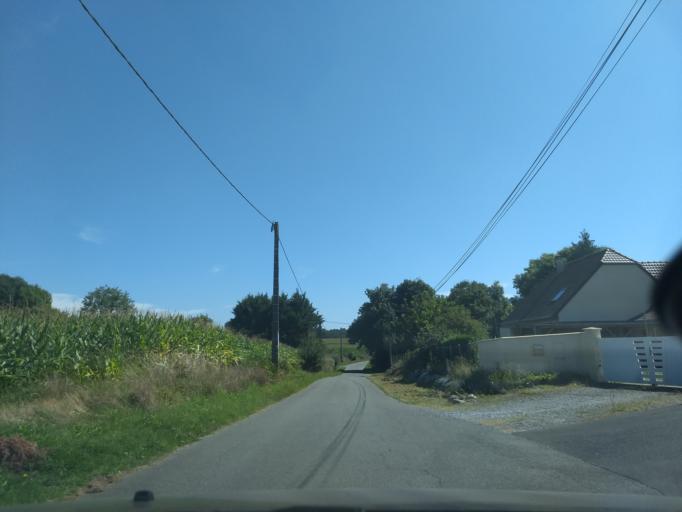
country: FR
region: Aquitaine
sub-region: Departement des Pyrenees-Atlantiques
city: Soumoulou
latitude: 43.2886
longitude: -0.1571
